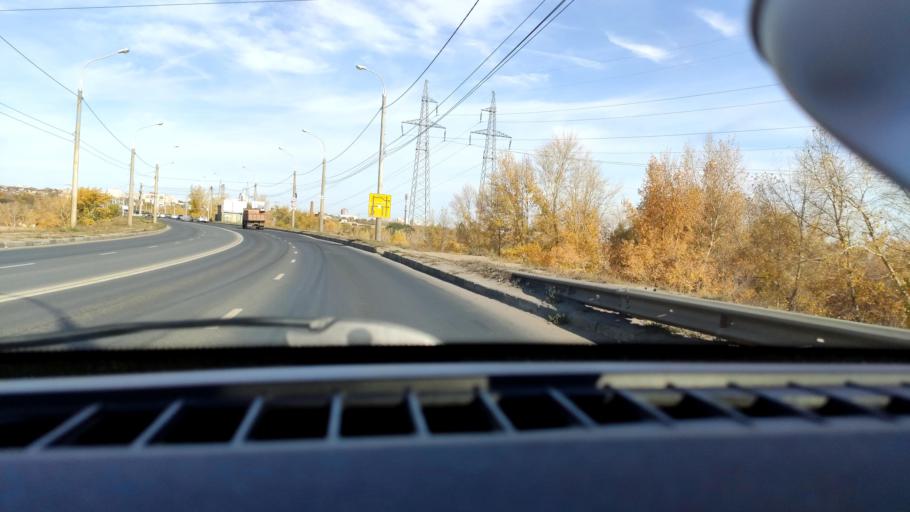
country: RU
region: Samara
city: Samara
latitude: 53.1653
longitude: 50.1970
